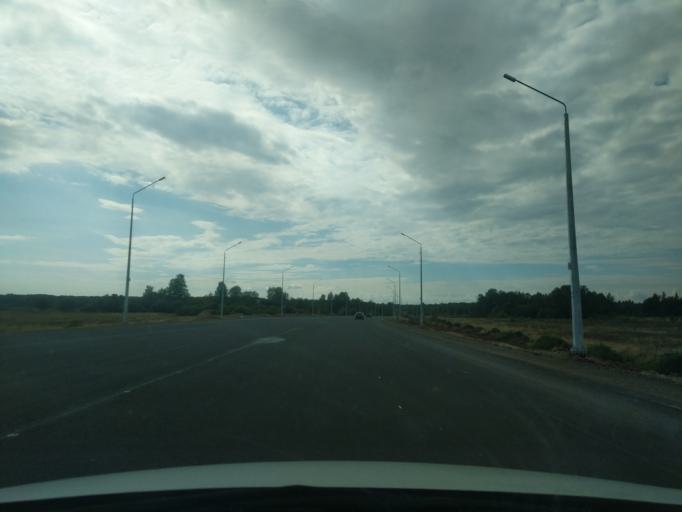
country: RU
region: Kostroma
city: Sudislavl'
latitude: 57.8292
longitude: 41.5385
